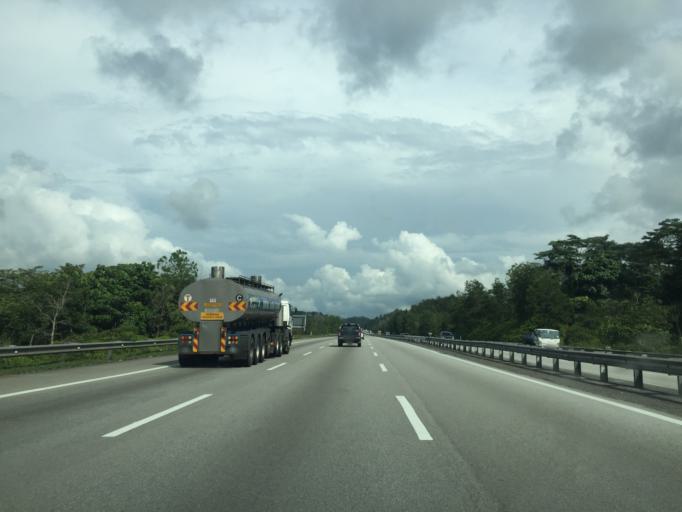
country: MY
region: Selangor
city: Serendah
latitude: 3.5216
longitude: 101.5253
